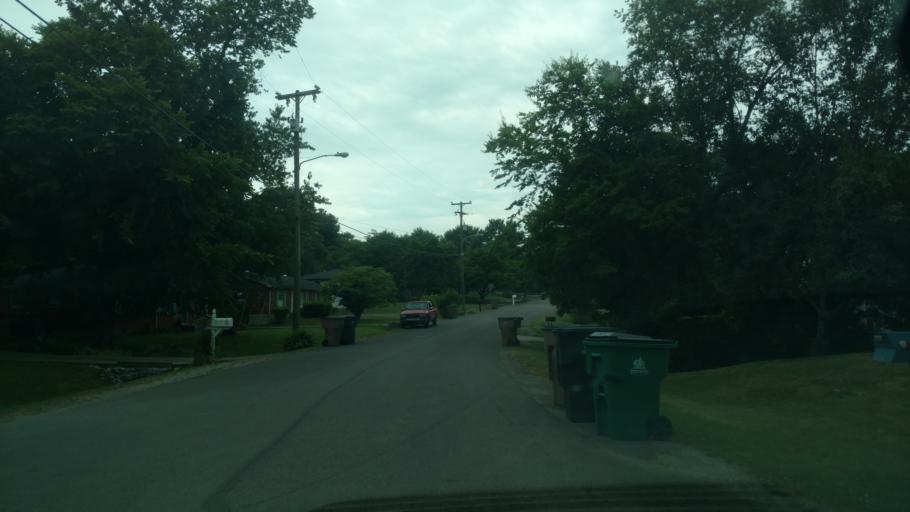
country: US
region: Tennessee
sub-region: Davidson County
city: Nashville
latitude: 36.1959
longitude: -86.7066
